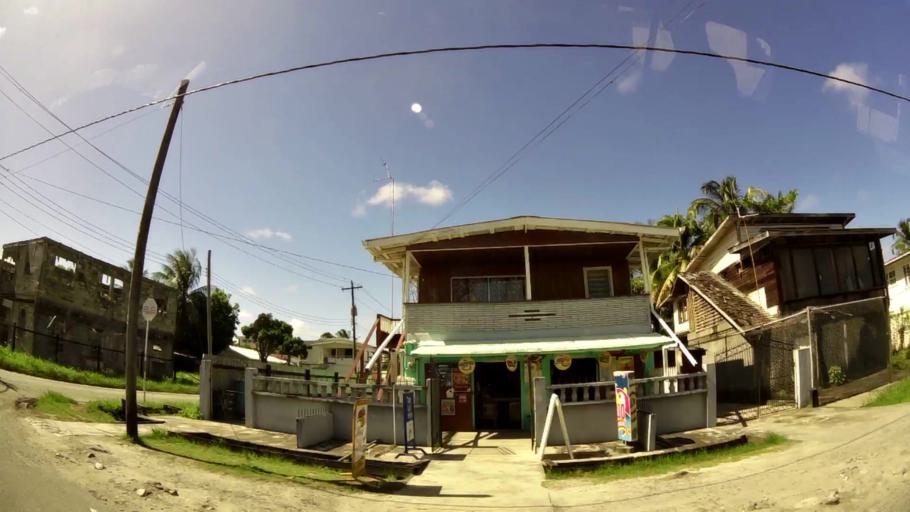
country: GY
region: Demerara-Mahaica
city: Georgetown
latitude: 6.8088
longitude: -58.1358
